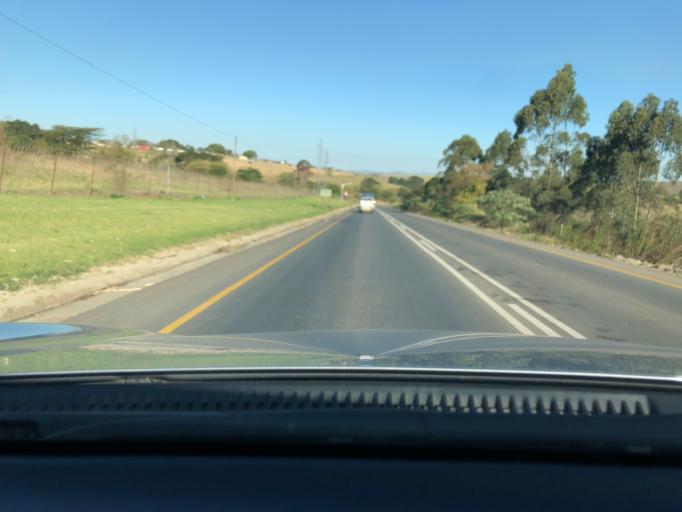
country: ZA
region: KwaZulu-Natal
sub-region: uMgungundlovu District Municipality
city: Camperdown
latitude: -29.7355
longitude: 30.5084
